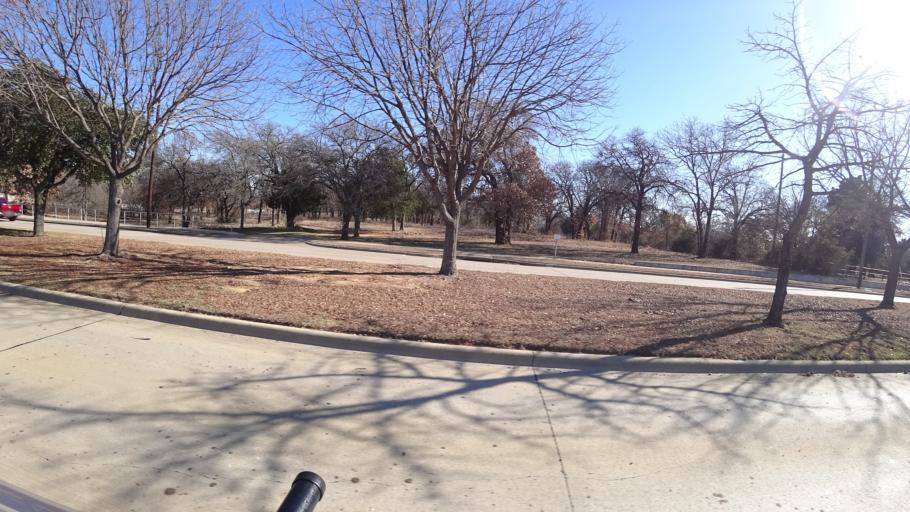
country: US
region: Texas
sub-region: Denton County
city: Lewisville
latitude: 33.0193
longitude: -97.0193
